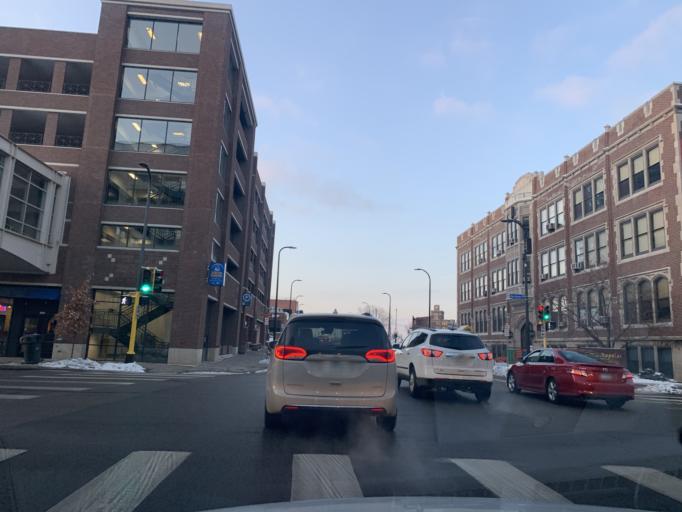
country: US
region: Minnesota
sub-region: Hennepin County
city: Minneapolis
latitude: 44.9742
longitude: -93.2783
